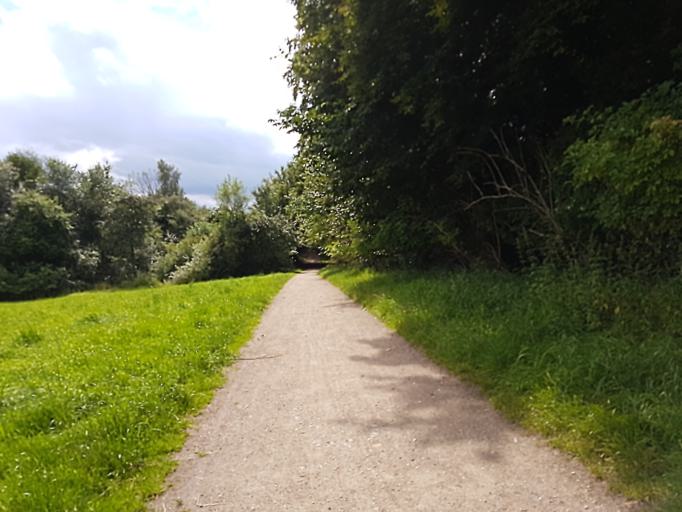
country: DK
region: Capital Region
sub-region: Fureso Kommune
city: Vaerlose
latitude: 55.7921
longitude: 12.3593
